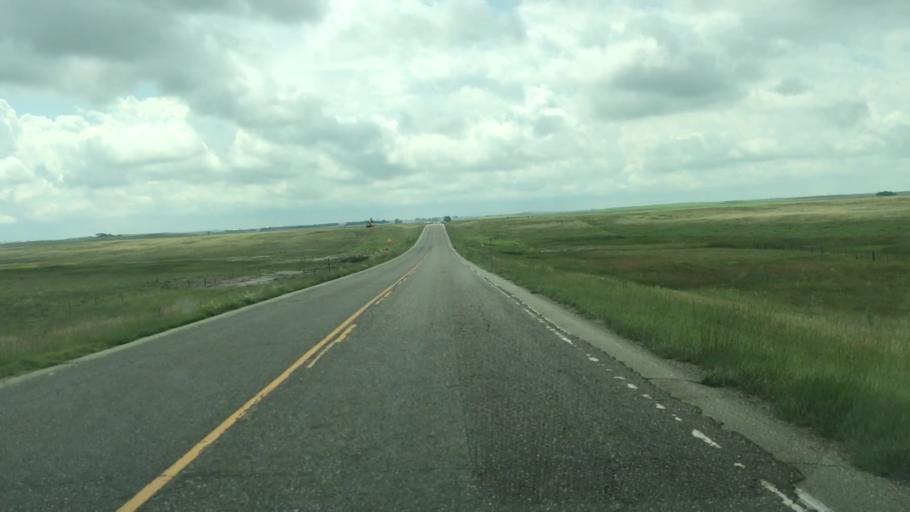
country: US
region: Nebraska
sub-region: Cherry County
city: Valentine
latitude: 43.0675
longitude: -100.5958
